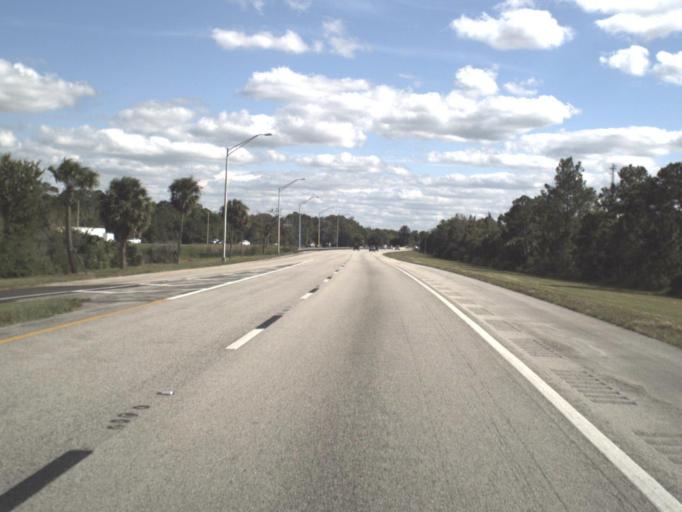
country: US
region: Florida
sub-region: Indian River County
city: Fellsmere
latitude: 27.5983
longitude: -80.8214
